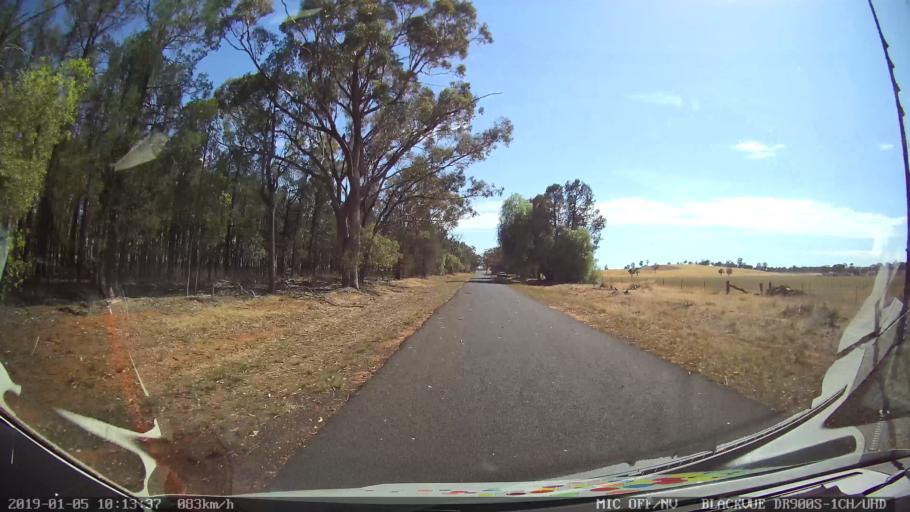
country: AU
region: New South Wales
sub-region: Gilgandra
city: Gilgandra
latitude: -31.6005
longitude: 148.9267
